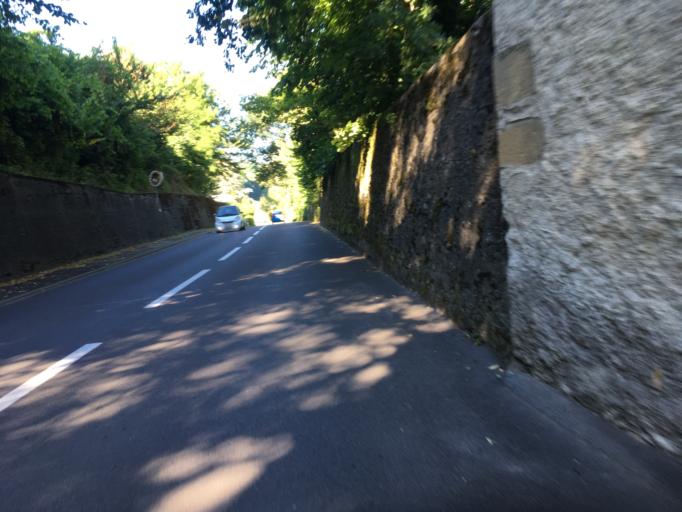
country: CH
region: Fribourg
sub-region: See District
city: Bas-Vully
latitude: 46.9388
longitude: 7.0584
